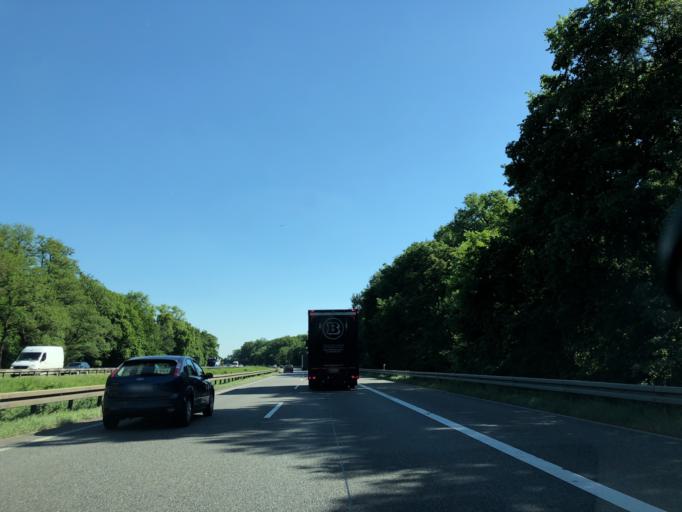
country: DE
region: Hesse
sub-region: Regierungsbezirk Darmstadt
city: Nauheim
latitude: 49.9454
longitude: 8.4775
